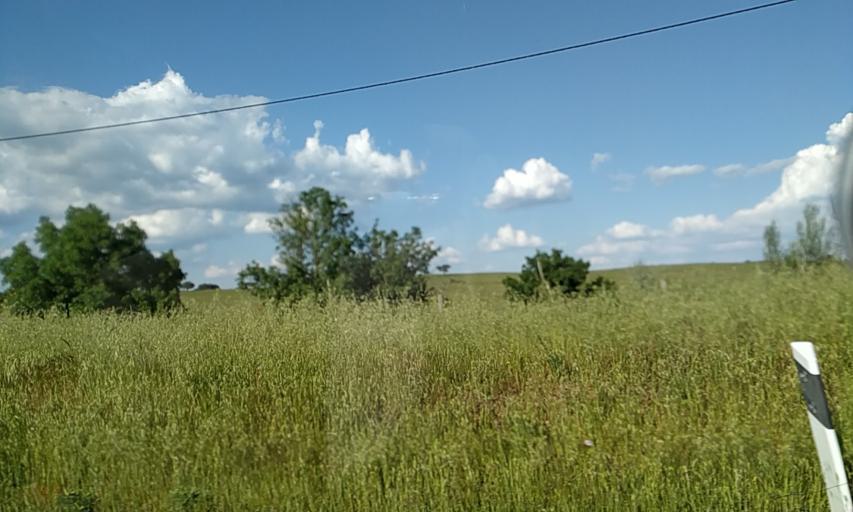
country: PT
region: Portalegre
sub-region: Portalegre
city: Urra
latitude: 39.1269
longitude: -7.4469
